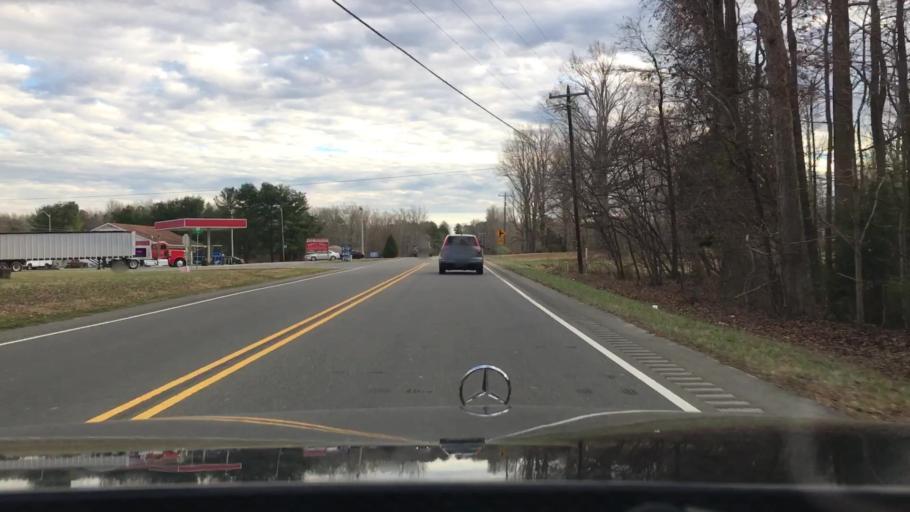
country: US
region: North Carolina
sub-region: Orange County
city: Hillsborough
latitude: 36.1374
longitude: -79.1208
